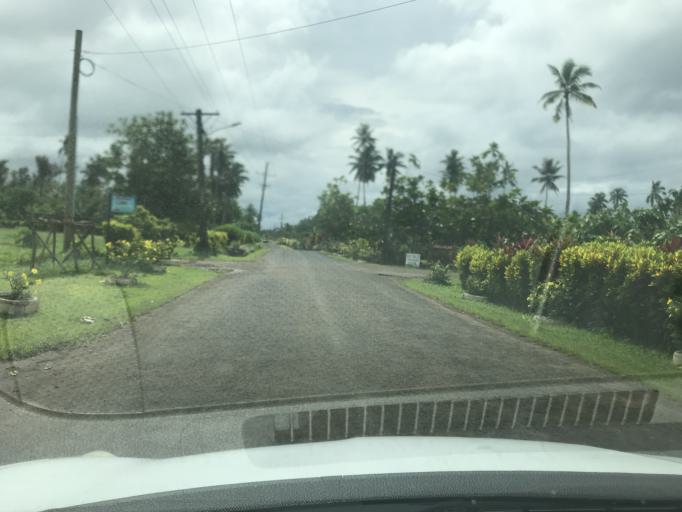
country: WS
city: Matavai
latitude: -14.0323
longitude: -171.6339
